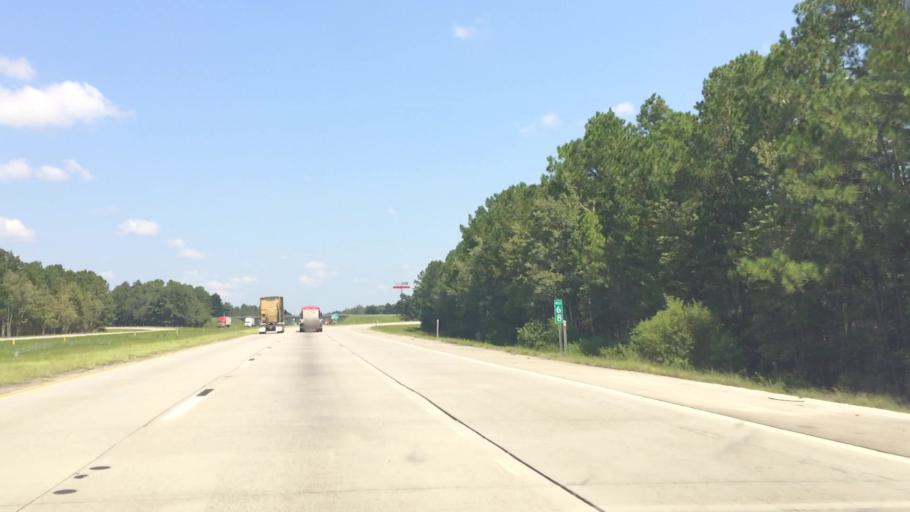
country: US
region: South Carolina
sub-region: Dorchester County
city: Saint George
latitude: 33.0794
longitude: -80.6551
